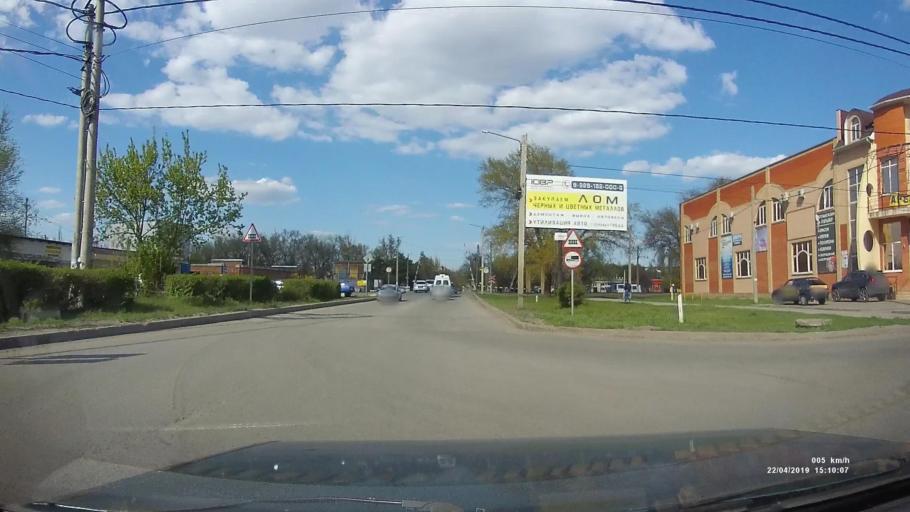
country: RU
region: Rostov
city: Azov
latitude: 47.0999
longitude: 39.4114
